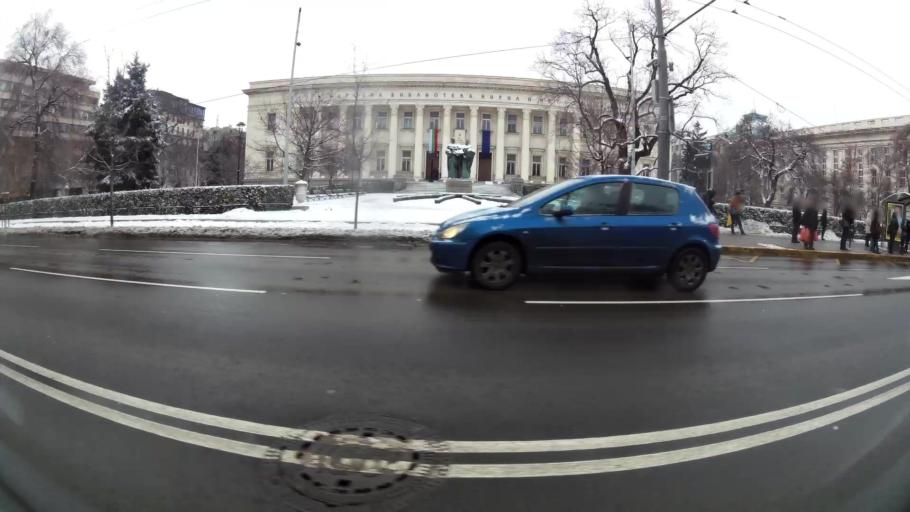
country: BG
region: Sofia-Capital
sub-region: Stolichna Obshtina
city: Sofia
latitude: 42.6949
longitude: 23.3349
